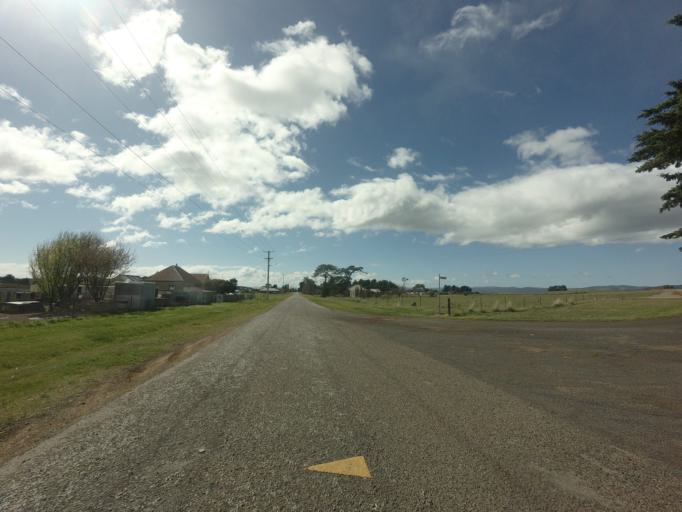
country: AU
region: Tasmania
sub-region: Northern Midlands
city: Evandale
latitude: -42.1452
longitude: 147.4190
